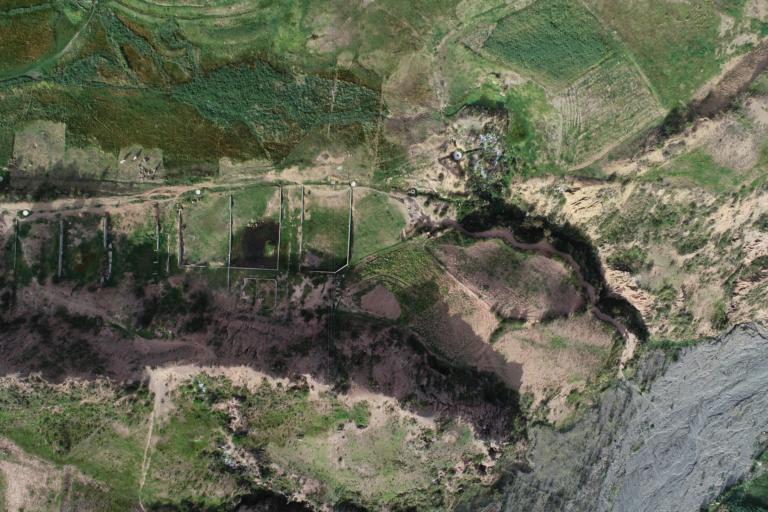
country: BO
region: La Paz
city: La Paz
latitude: -16.5475
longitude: -68.0024
